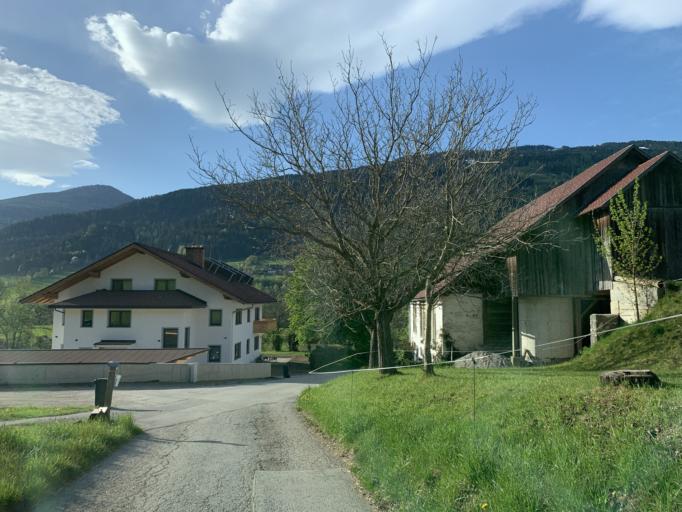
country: AT
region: Styria
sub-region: Politischer Bezirk Liezen
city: Schladming
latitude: 47.4047
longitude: 13.7070
